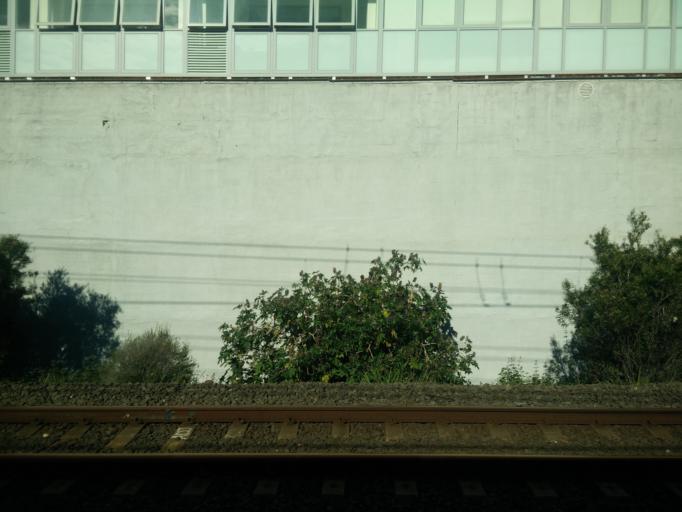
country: AU
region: New South Wales
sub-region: Ashfield
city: Croydon
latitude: -33.8769
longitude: 151.1021
